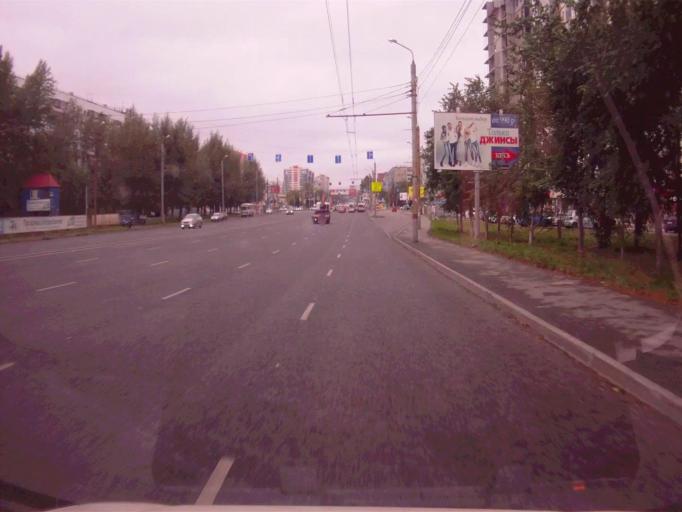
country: RU
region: Chelyabinsk
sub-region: Gorod Chelyabinsk
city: Chelyabinsk
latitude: 55.1774
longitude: 61.3327
